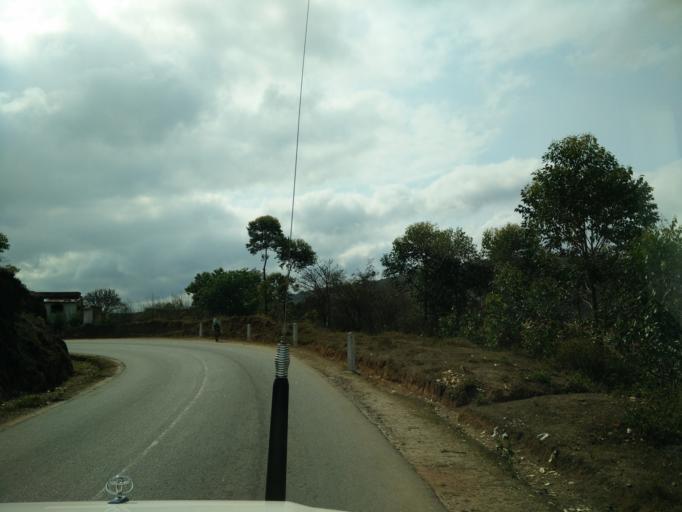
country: MG
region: Upper Matsiatra
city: Fianarantsoa
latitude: -21.3624
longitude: 47.1785
